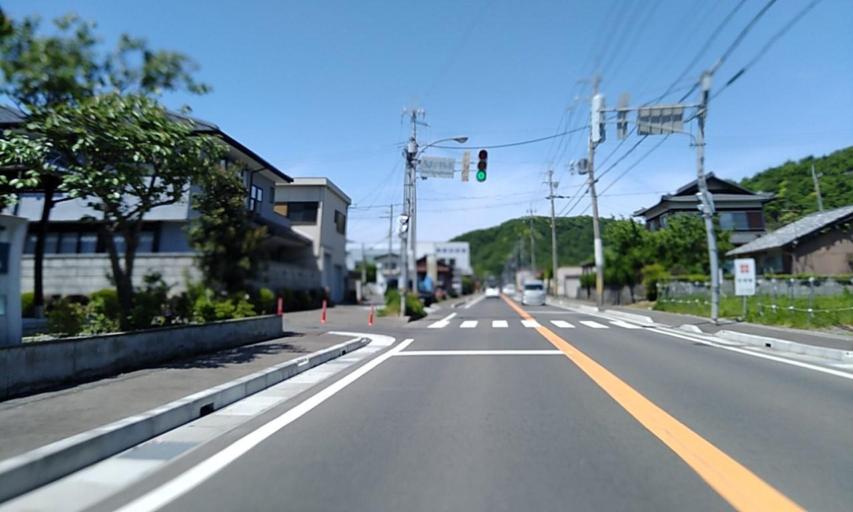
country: JP
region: Fukui
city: Obama
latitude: 35.5138
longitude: 135.7530
